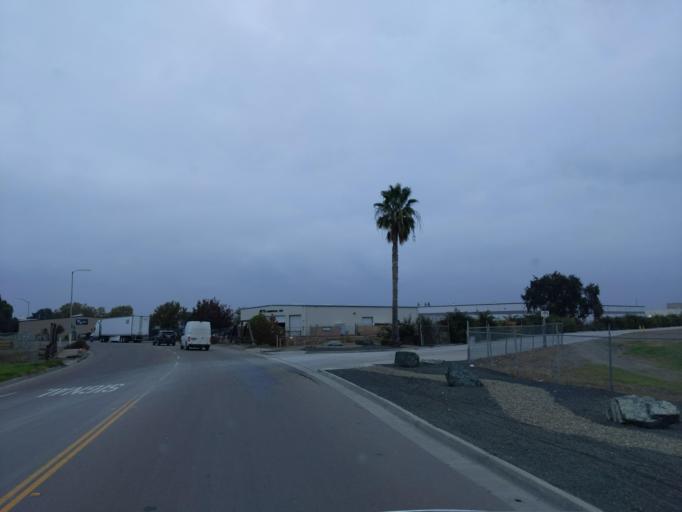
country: US
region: California
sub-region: San Joaquin County
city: Kennedy
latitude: 37.9325
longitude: -121.2279
